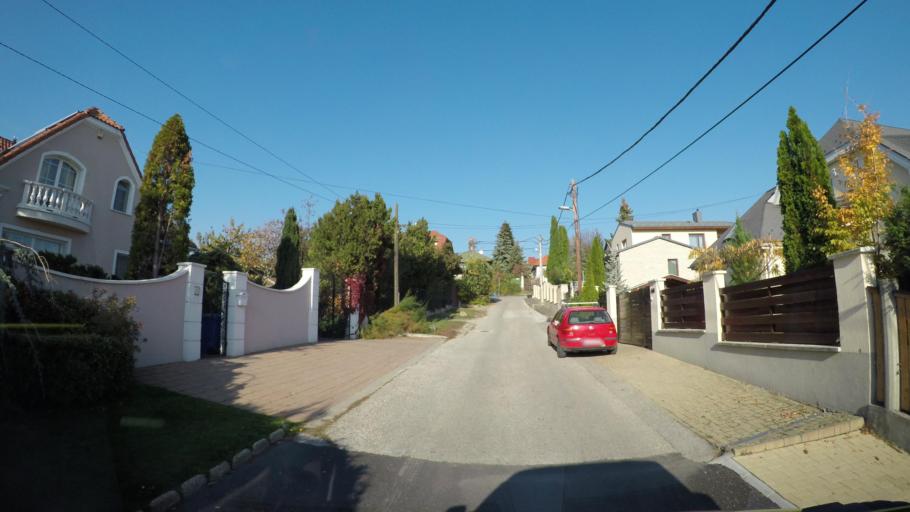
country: HU
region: Pest
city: Szentendre
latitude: 47.6873
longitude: 19.0699
